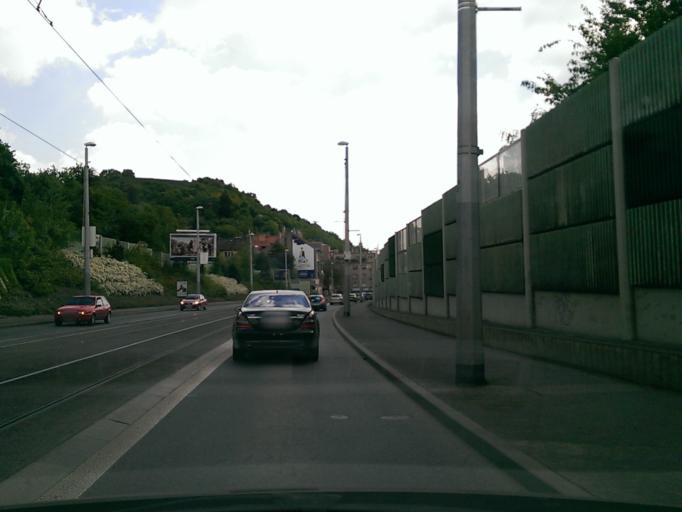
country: CZ
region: Praha
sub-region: Praha 2
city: Vysehrad
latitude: 50.0605
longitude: 14.3954
